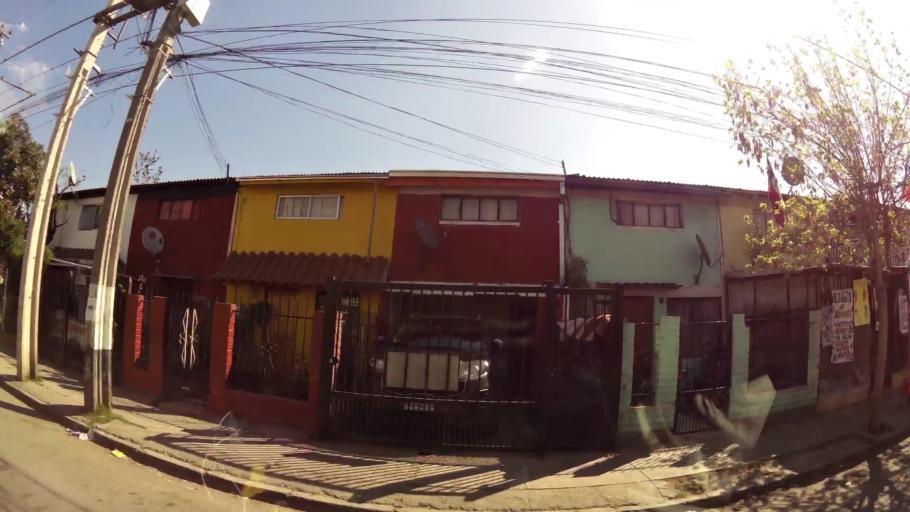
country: CL
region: Santiago Metropolitan
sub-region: Provincia de Santiago
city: La Pintana
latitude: -33.5604
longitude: -70.6253
